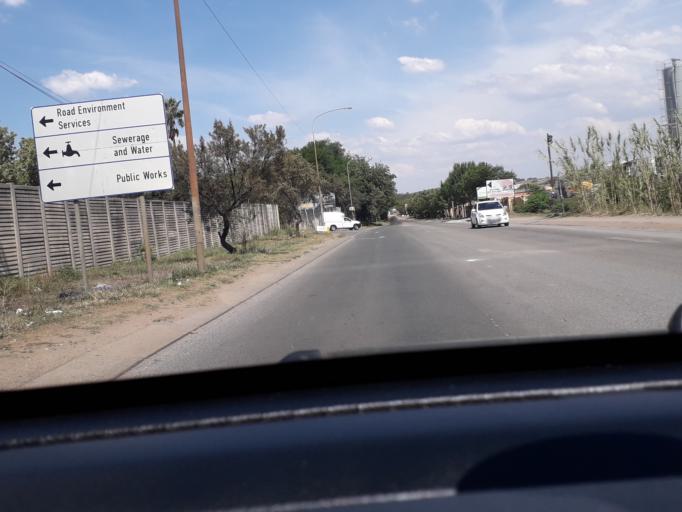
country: ZA
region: Gauteng
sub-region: City of Tshwane Metropolitan Municipality
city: Centurion
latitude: -25.8435
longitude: 28.2177
